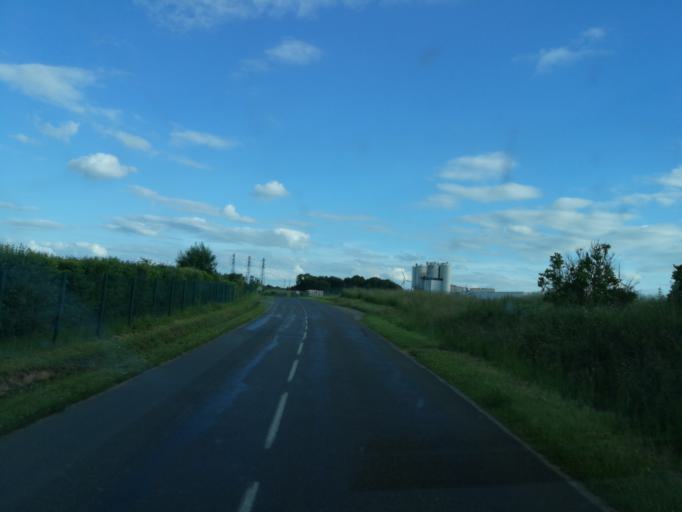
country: FR
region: Haute-Normandie
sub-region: Departement de l'Eure
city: Damville
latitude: 48.8635
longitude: 1.0731
